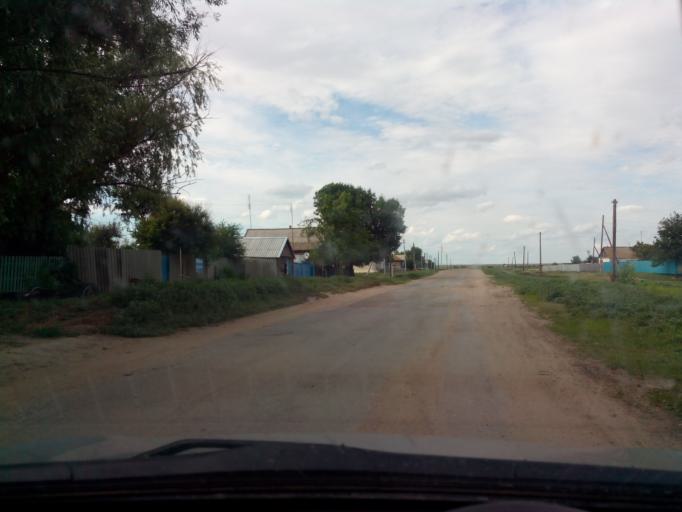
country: RU
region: Volgograd
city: Leninsk
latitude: 48.6679
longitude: 45.3680
